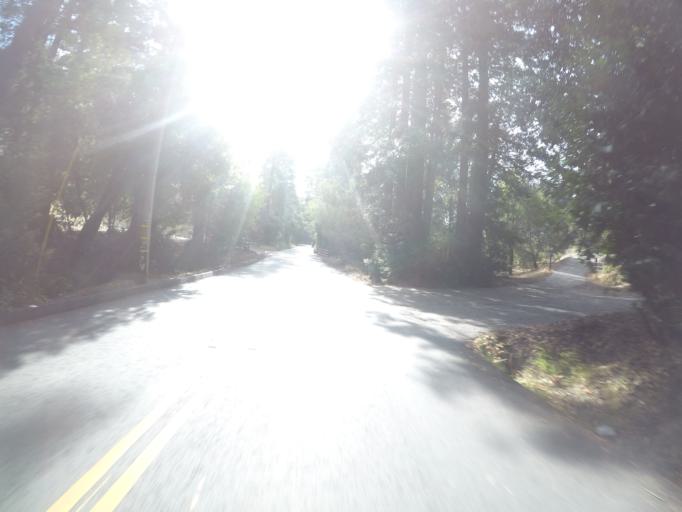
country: US
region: California
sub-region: Santa Cruz County
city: Scotts Valley
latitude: 37.0360
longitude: -121.9969
